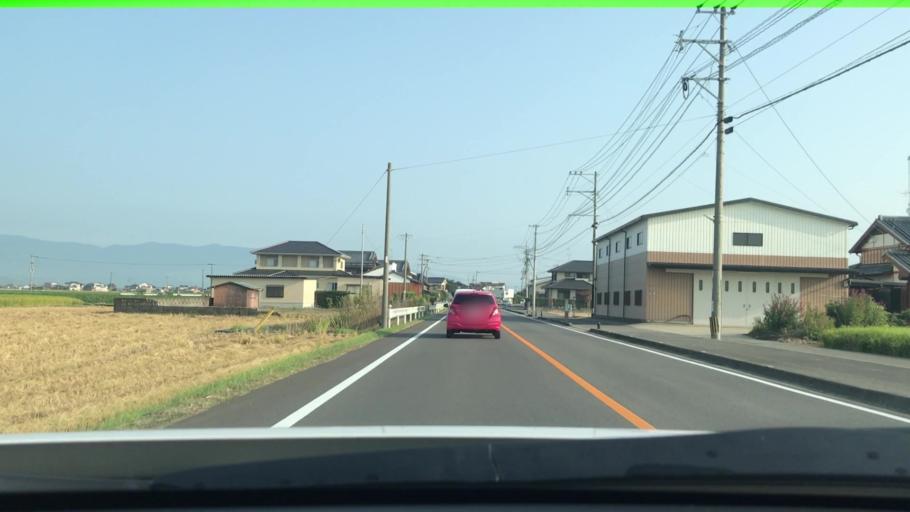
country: JP
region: Saga Prefecture
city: Saga-shi
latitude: 33.2066
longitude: 130.2061
